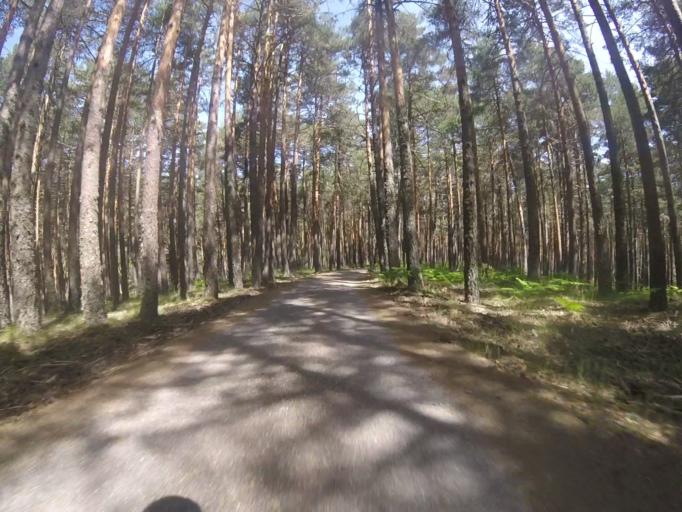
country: ES
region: Madrid
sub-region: Provincia de Madrid
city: Cercedilla
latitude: 40.8157
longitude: -4.0291
